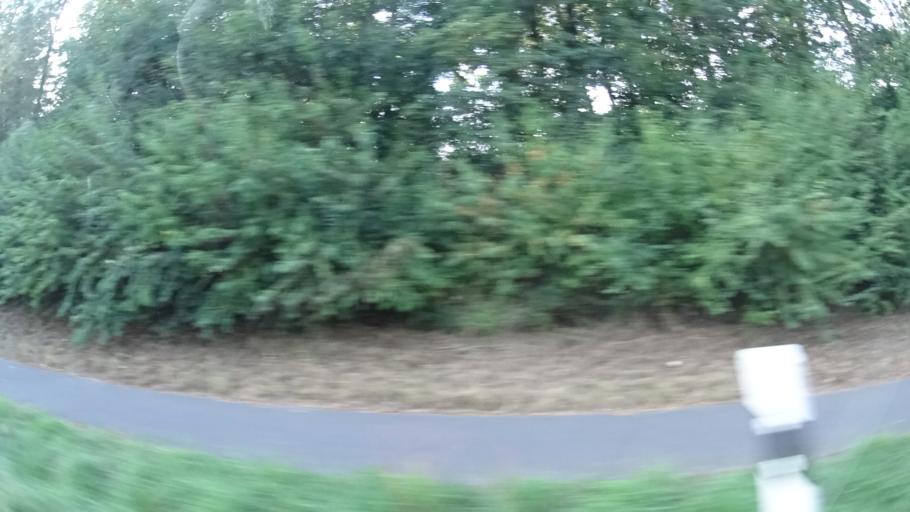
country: DE
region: Hesse
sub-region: Regierungsbezirk Kassel
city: Neuhof
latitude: 50.4603
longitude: 9.6204
